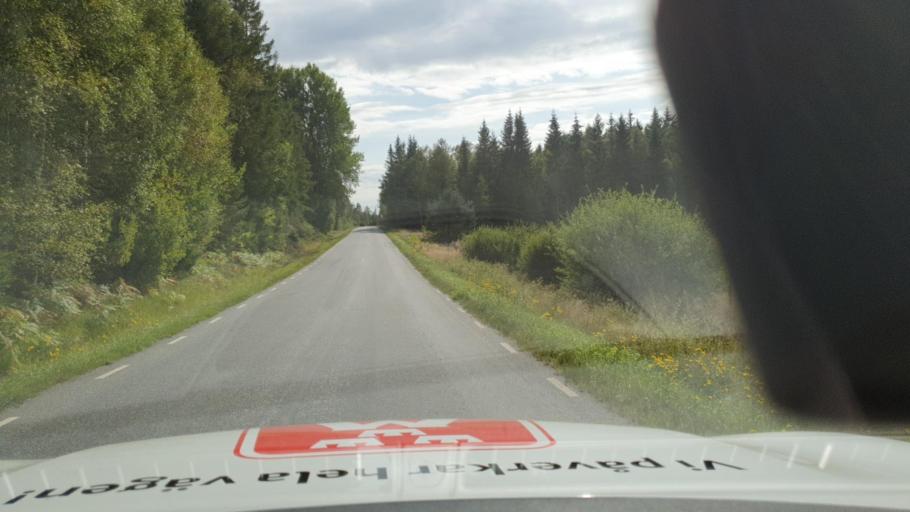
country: SE
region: Vaestra Goetaland
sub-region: Marks Kommun
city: Kinna
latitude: 57.3903
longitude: 12.7715
